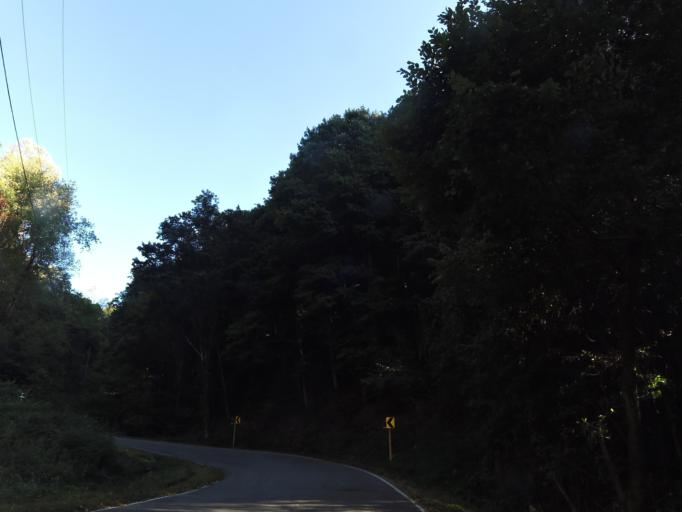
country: US
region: Tennessee
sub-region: Union County
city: Luttrell
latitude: 36.2435
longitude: -83.6490
